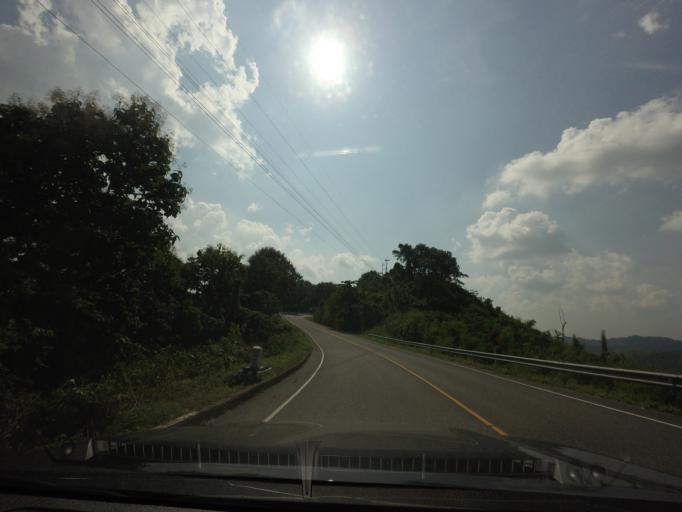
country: TH
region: Nan
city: Santi Suk
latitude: 18.9740
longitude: 101.0316
